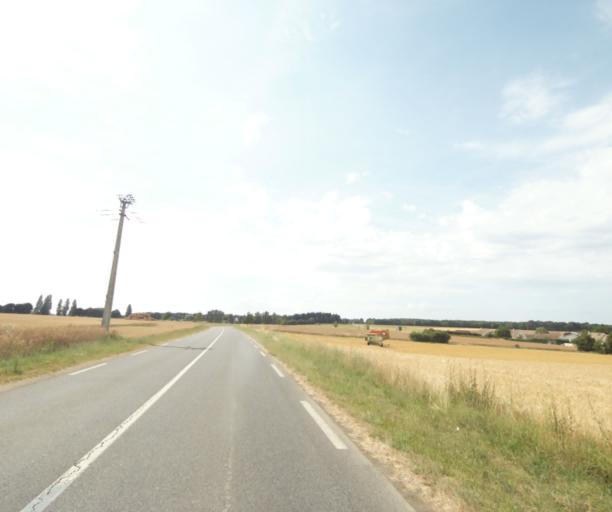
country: FR
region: Ile-de-France
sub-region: Departement de Seine-et-Marne
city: Acheres-la-Foret
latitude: 48.3406
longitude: 2.5977
